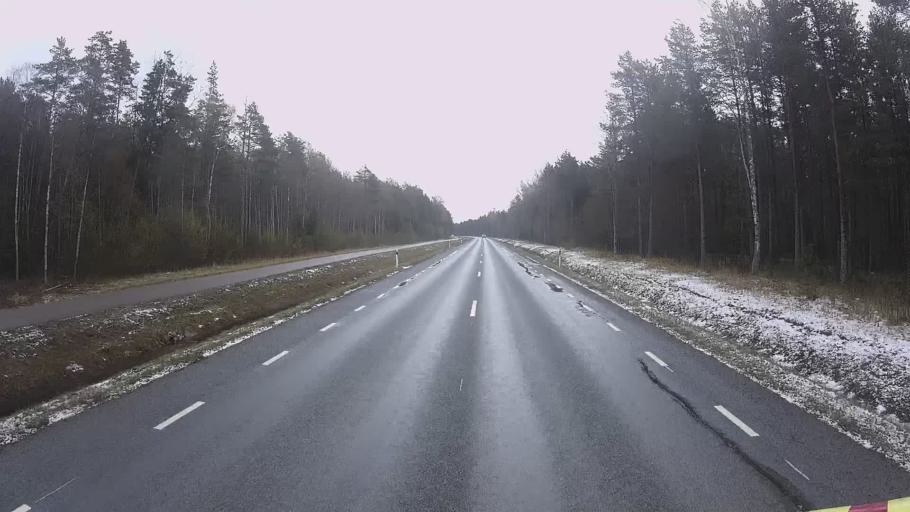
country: EE
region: Hiiumaa
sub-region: Kaerdla linn
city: Kardla
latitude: 58.9999
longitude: 22.7015
